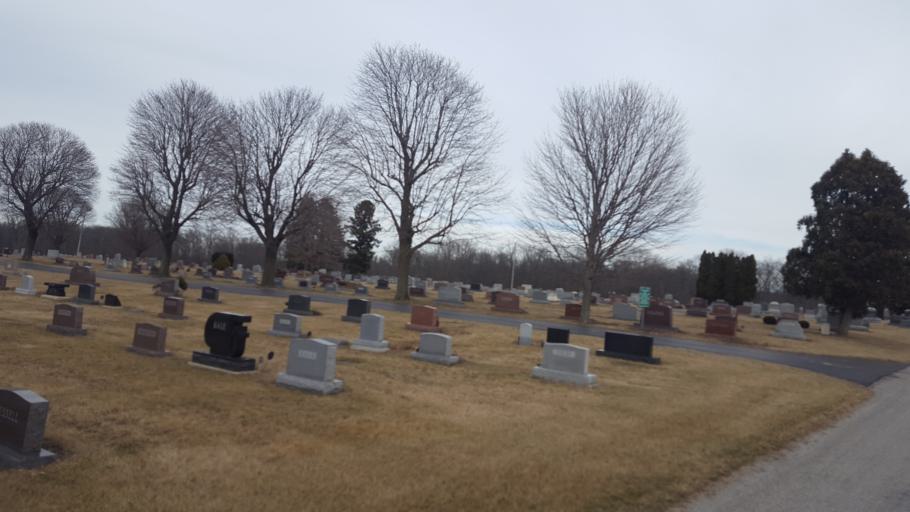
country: US
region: Ohio
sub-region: Union County
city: Richwood
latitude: 40.4946
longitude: -83.3258
